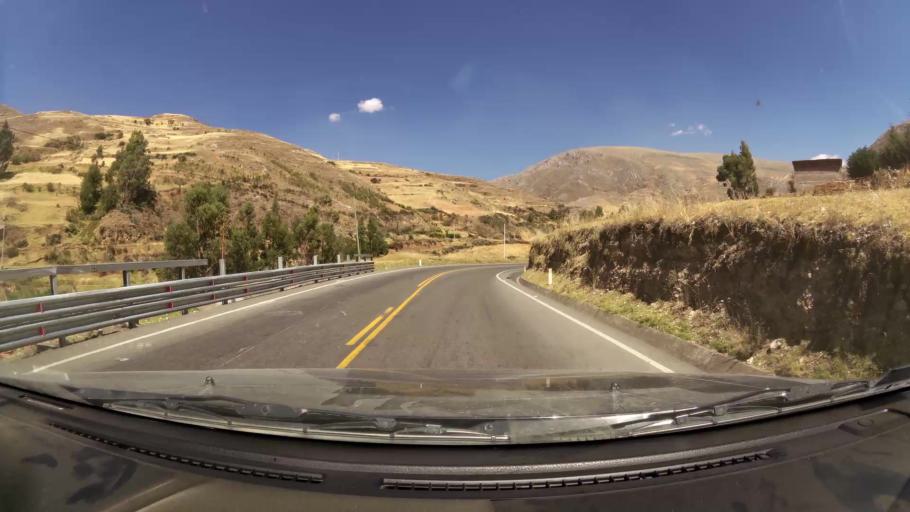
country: PE
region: Junin
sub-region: Provincia de Jauja
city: Llocllapampa
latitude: -11.8022
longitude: -75.5948
